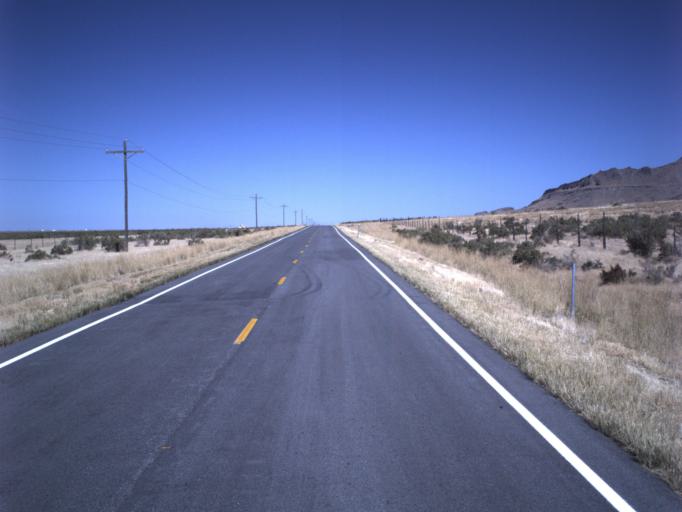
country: US
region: Utah
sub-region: Tooele County
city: Grantsville
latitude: 40.6925
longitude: -112.6679
